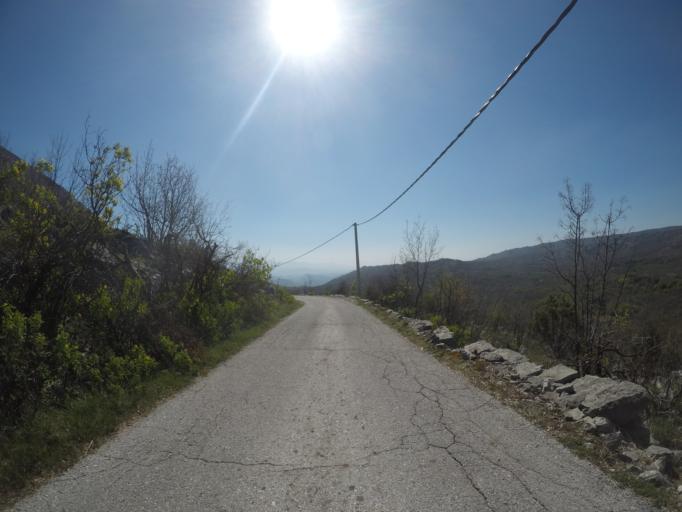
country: ME
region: Danilovgrad
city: Danilovgrad
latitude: 42.5295
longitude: 19.0296
